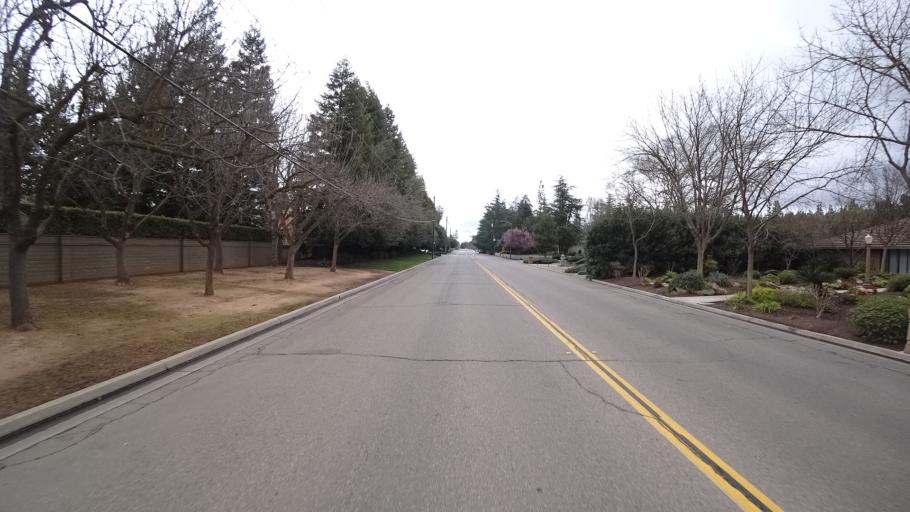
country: US
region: California
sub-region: Fresno County
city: Fresno
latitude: 36.8445
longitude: -119.8299
